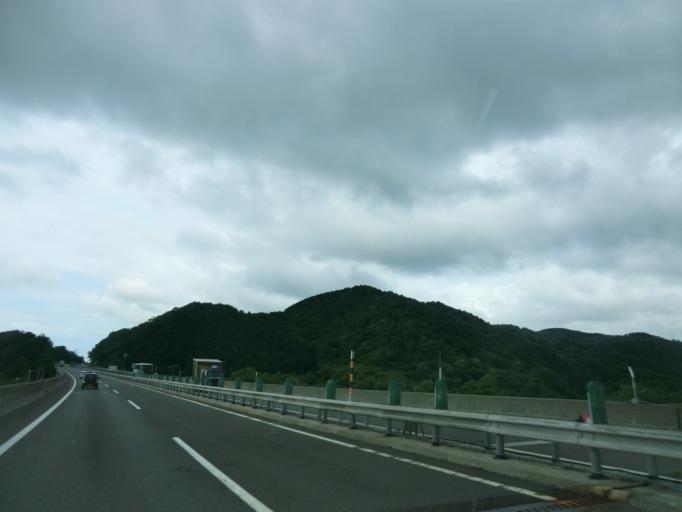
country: JP
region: Hokkaido
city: Sunagawa
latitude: 43.4155
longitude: 141.9109
